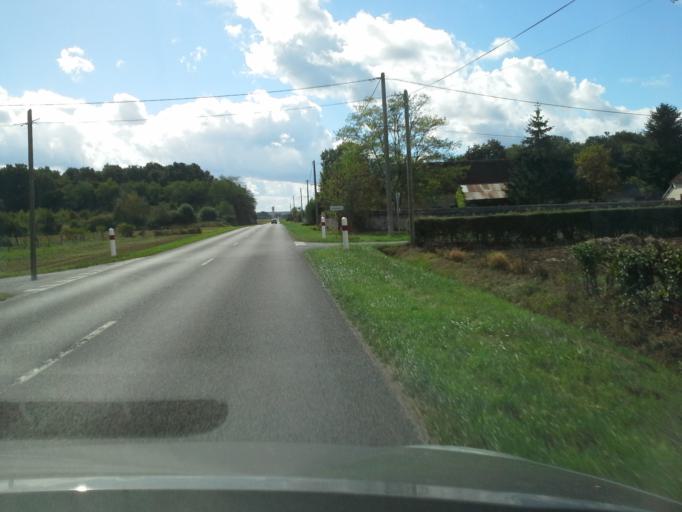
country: FR
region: Centre
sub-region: Departement du Loir-et-Cher
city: Pontlevoy
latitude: 47.4162
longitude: 1.2760
